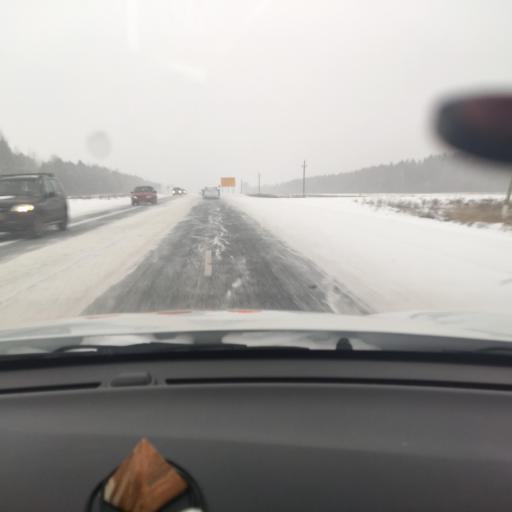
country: RU
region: Tatarstan
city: Sviyazhsk
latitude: 55.7310
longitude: 48.8034
